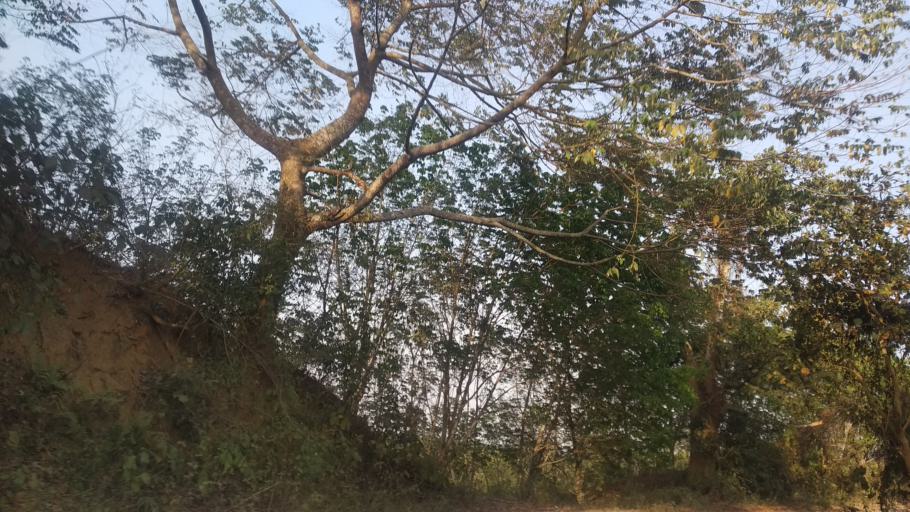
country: IN
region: Tripura
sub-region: West Tripura
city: Sonamura
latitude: 23.4373
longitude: 91.3595
